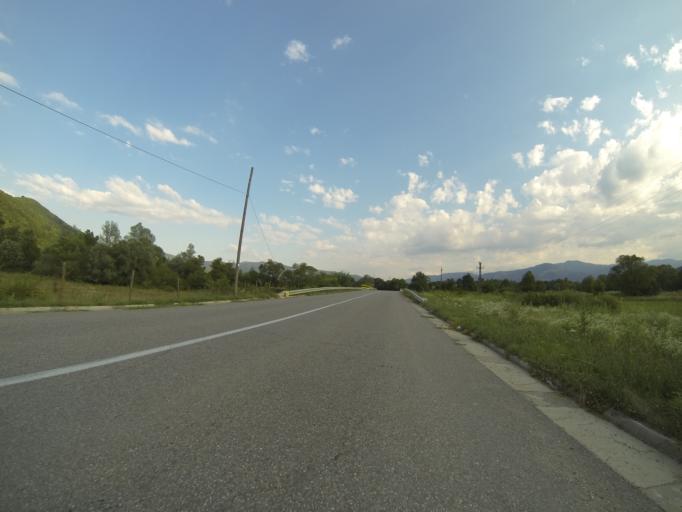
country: RO
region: Brasov
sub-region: Comuna Sinca Noua
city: Sinca Noua
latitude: 45.7356
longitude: 25.2299
